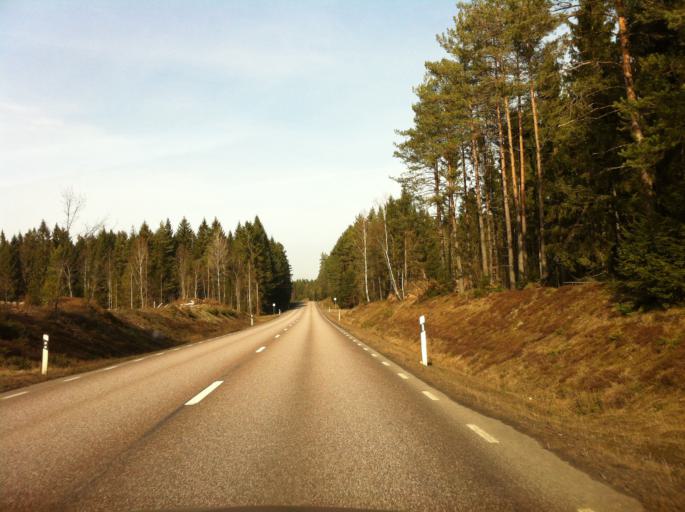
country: SE
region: Vaestra Goetaland
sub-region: Skovde Kommun
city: Skultorp
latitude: 58.2710
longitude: 13.8099
